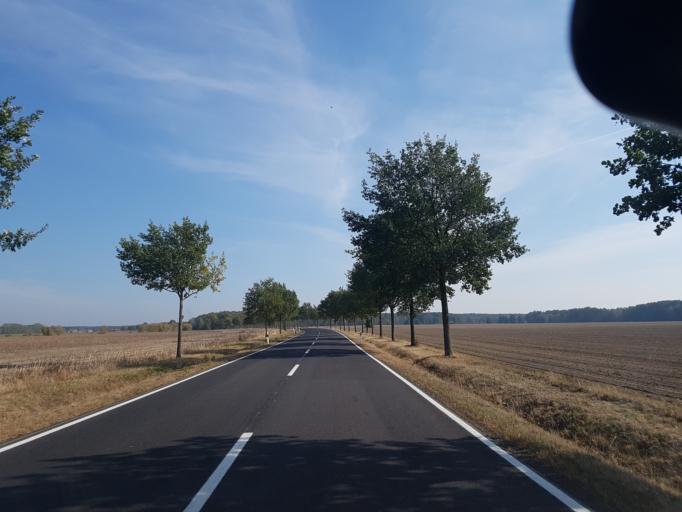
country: DE
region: Brandenburg
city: Ihlow
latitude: 51.8251
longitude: 13.3659
